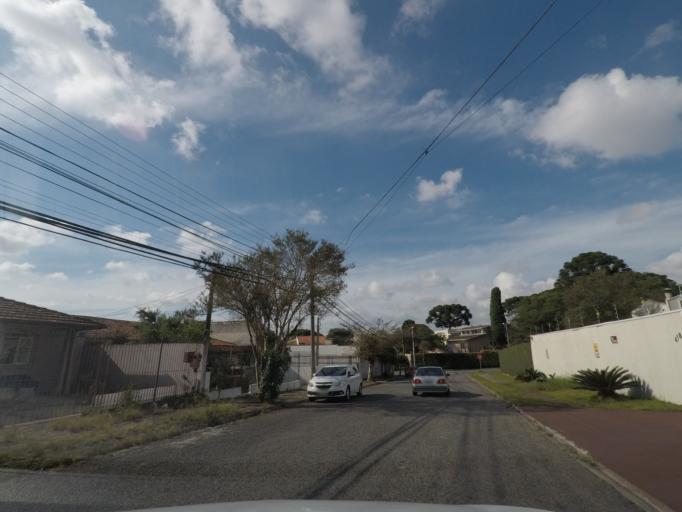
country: BR
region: Parana
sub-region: Pinhais
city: Pinhais
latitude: -25.4584
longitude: -49.2342
